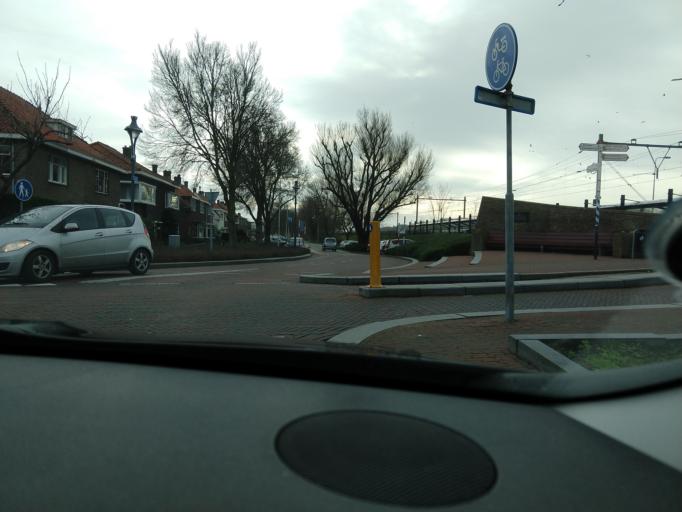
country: NL
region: Zeeland
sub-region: Gemeente Vlissingen
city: Vlissingen
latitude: 51.4647
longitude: 3.5956
